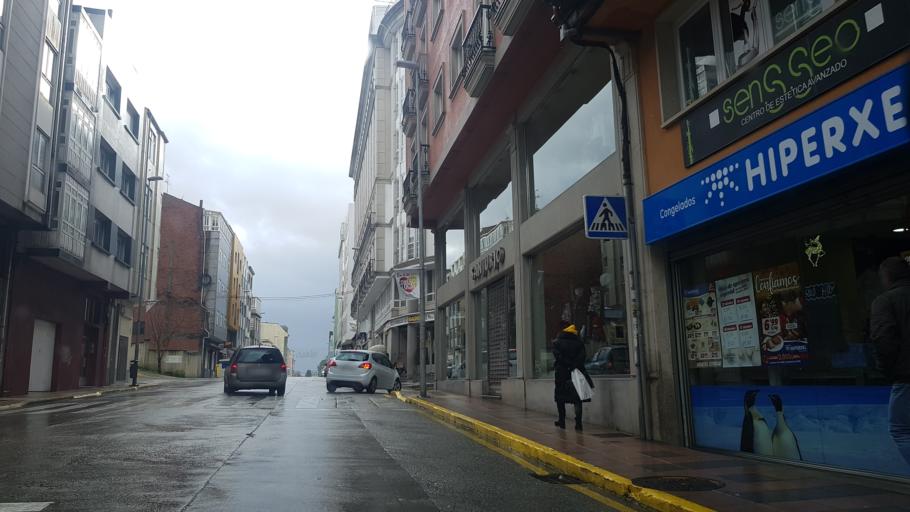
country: ES
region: Galicia
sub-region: Provincia de Lugo
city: Vilalba
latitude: 43.2969
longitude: -7.6818
